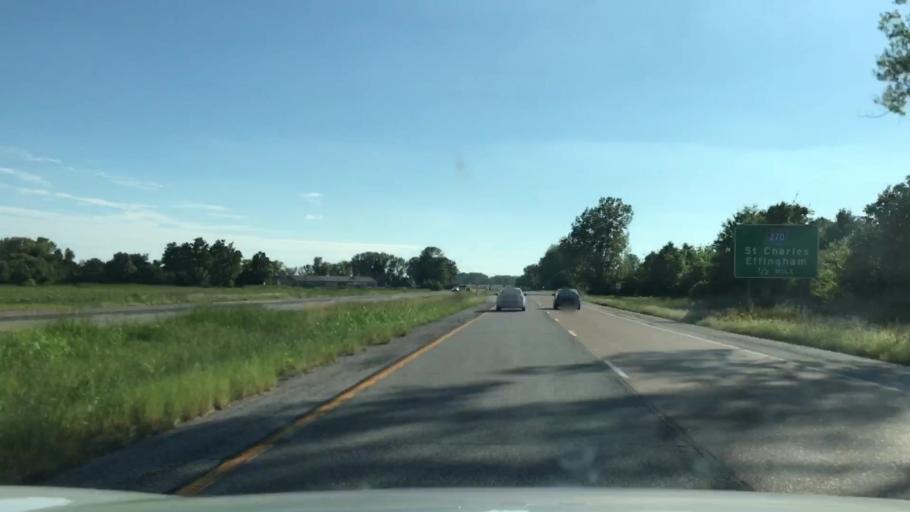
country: US
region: Illinois
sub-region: Madison County
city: Mitchell
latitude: 38.7752
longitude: -90.1163
